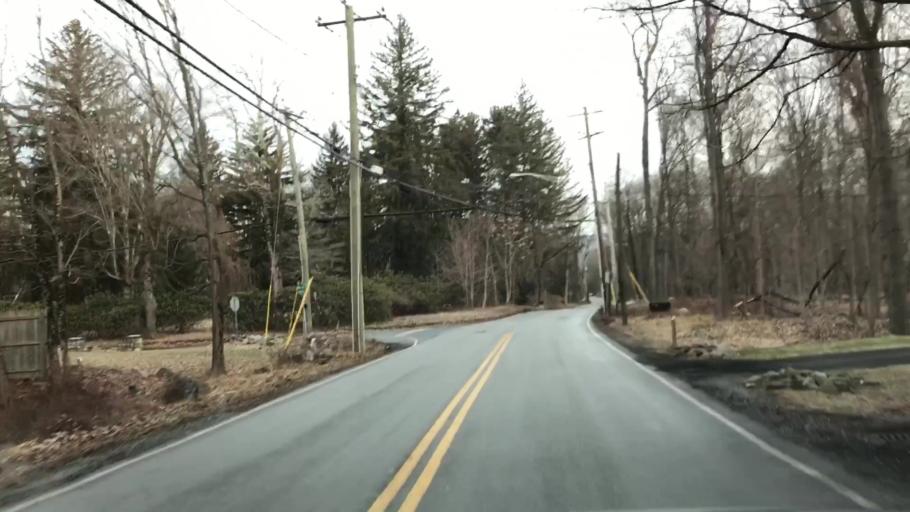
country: US
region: New York
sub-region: Rockland County
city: Viola
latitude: 41.1373
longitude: -74.0970
